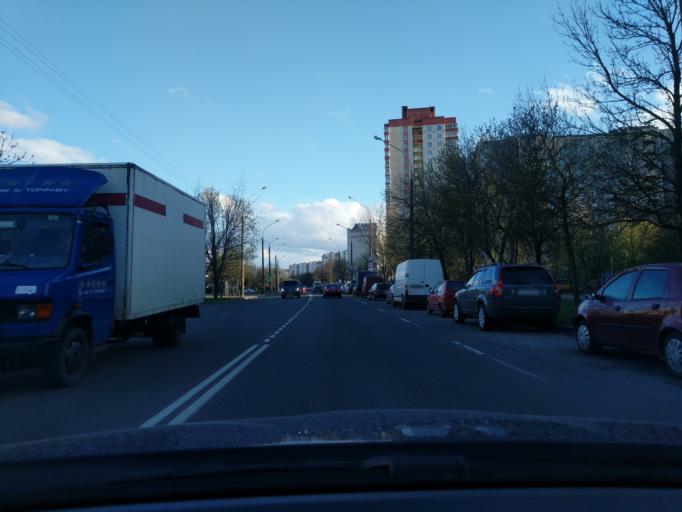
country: BY
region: Minsk
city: Novoye Medvezhino
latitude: 53.9155
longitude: 27.4498
